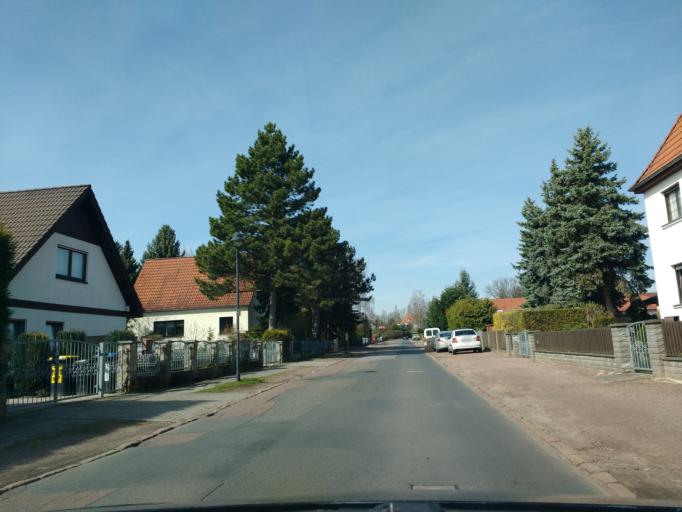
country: DE
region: Saxony-Anhalt
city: Halle (Saale)
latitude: 51.4966
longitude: 12.0226
